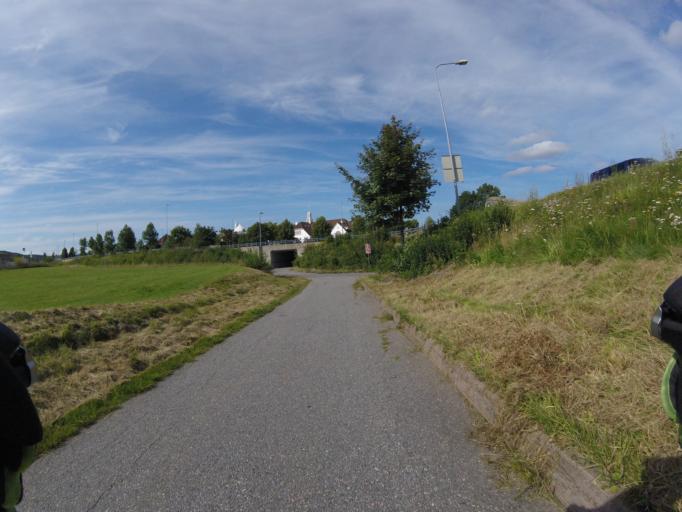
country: NO
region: Akershus
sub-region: Skedsmo
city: Lillestrom
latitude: 59.9780
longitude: 11.0009
